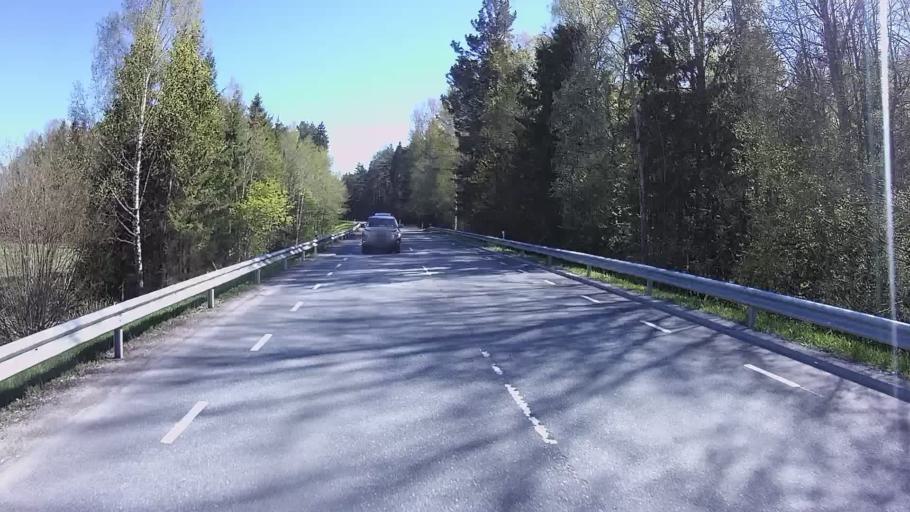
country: EE
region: Harju
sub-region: Loksa linn
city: Loksa
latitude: 59.5585
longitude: 25.7246
